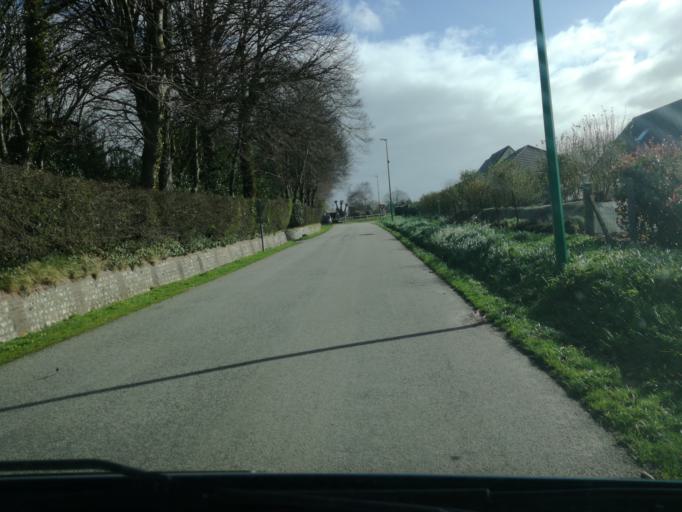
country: FR
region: Haute-Normandie
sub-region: Departement de la Seine-Maritime
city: Yport
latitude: 49.7380
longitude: 0.3332
